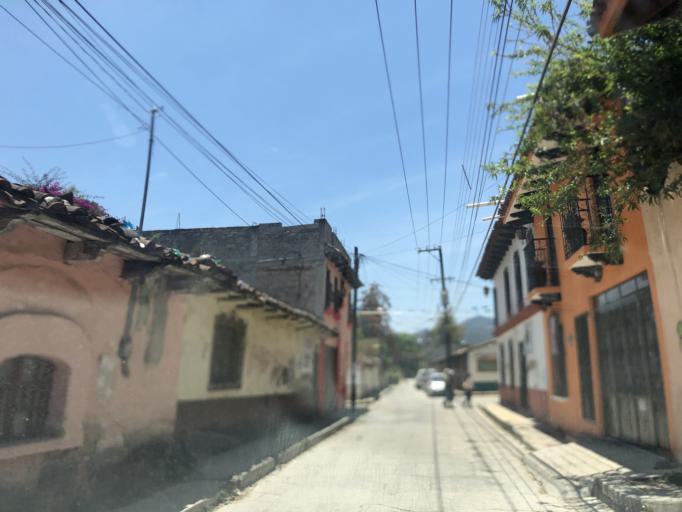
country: MX
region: Chiapas
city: San Cristobal de las Casas
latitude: 16.7313
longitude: -92.6420
